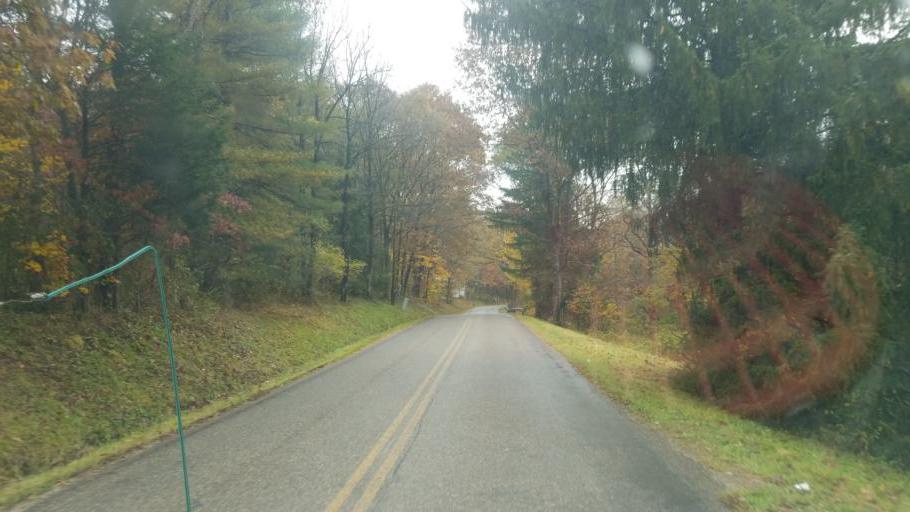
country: US
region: Ohio
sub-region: Washington County
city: Beverly
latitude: 39.5505
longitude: -81.6651
